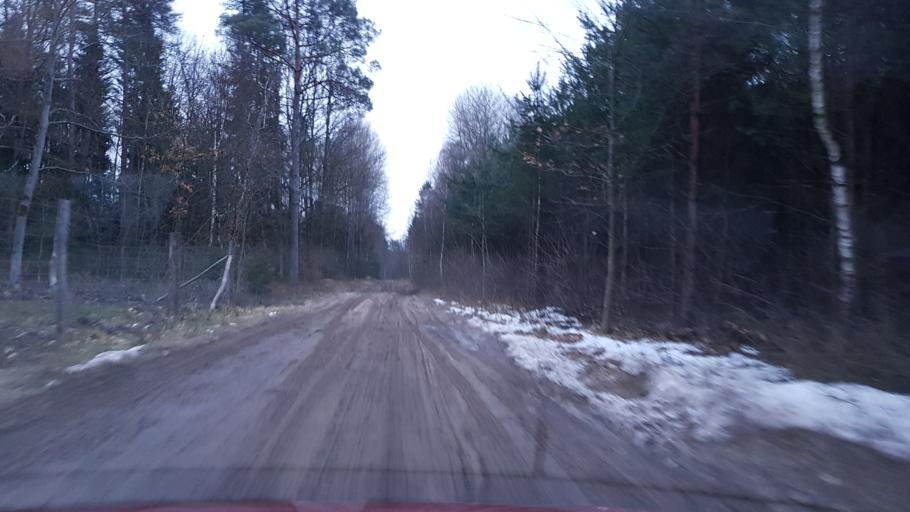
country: PL
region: Greater Poland Voivodeship
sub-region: Powiat zlotowski
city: Sypniewo
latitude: 53.4921
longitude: 16.6852
